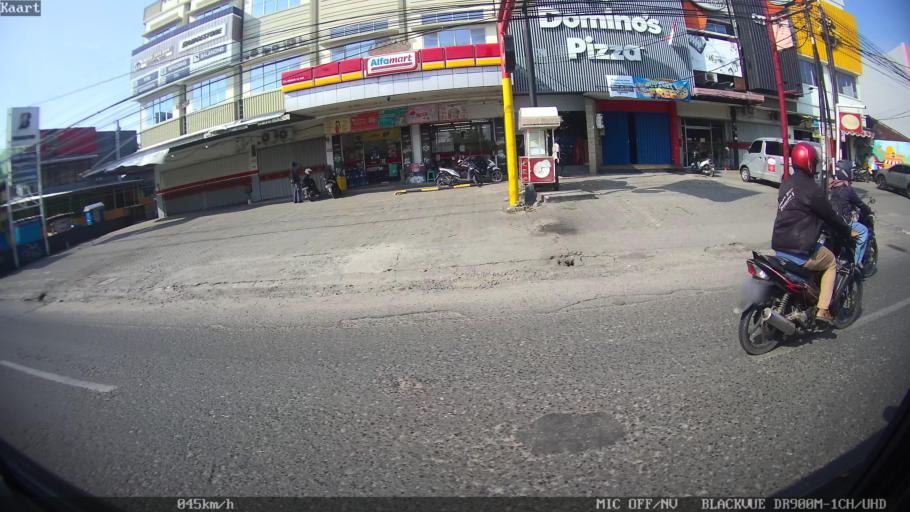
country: ID
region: Lampung
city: Kedaton
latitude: -5.3816
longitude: 105.2569
